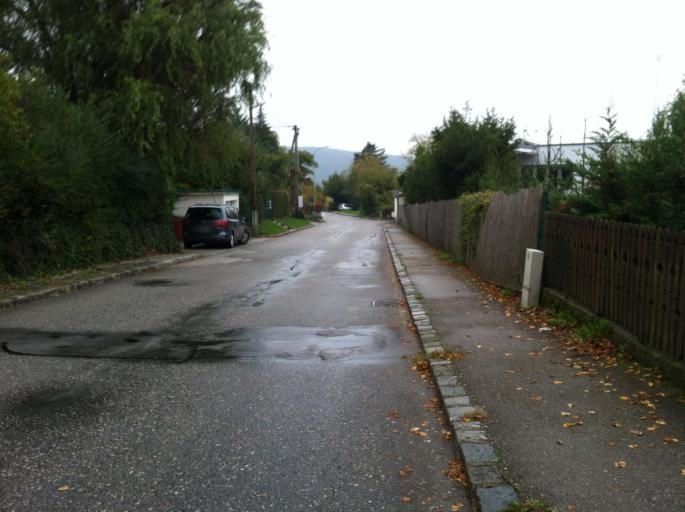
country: AT
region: Lower Austria
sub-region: Politischer Bezirk Wien-Umgebung
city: Gablitz
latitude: 48.2220
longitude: 16.1477
